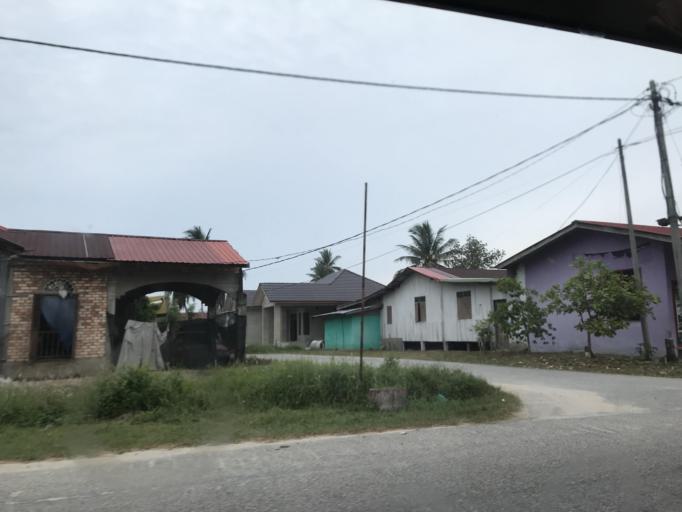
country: MY
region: Kelantan
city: Kota Bharu
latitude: 6.1681
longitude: 102.2086
